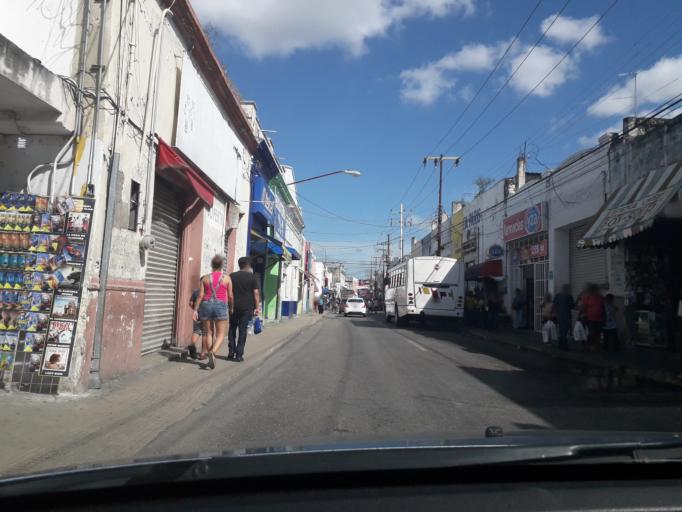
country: MX
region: Yucatan
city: Merida
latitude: 20.9636
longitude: -89.6244
